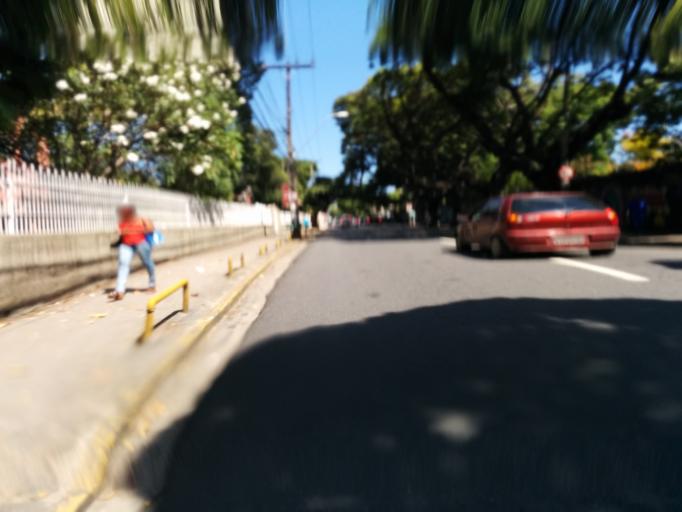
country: BR
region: Pernambuco
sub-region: Recife
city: Recife
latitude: -8.0554
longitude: -34.8886
